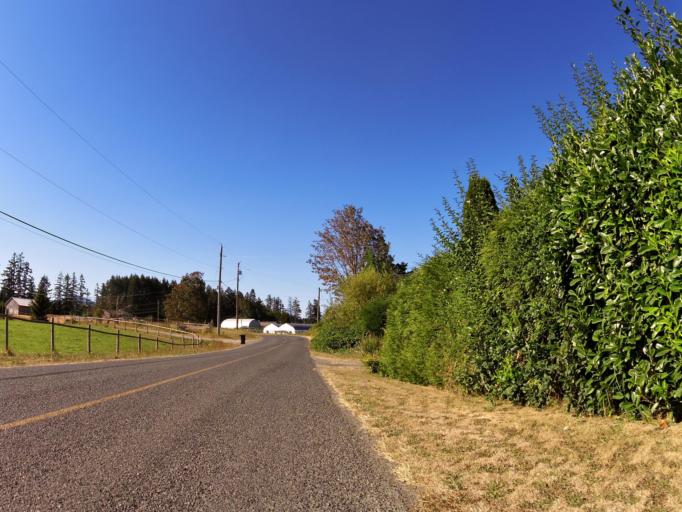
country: CA
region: British Columbia
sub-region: Cowichan Valley Regional District
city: Ladysmith
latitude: 49.0787
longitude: -123.8401
